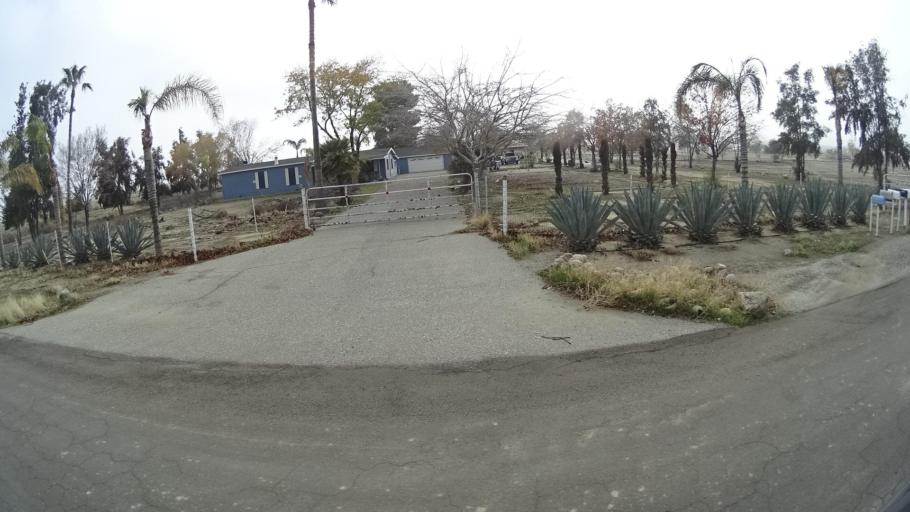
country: US
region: California
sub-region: Kern County
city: Maricopa
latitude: 35.0471
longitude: -119.3539
